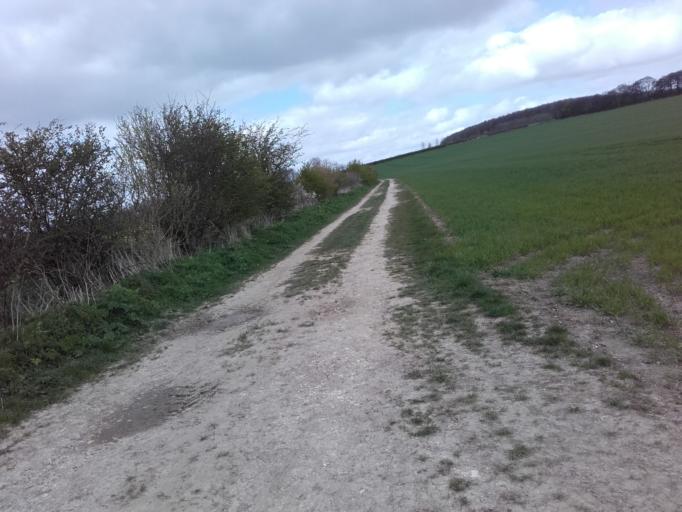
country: GB
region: England
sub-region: East Riding of Yorkshire
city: Market Weighton
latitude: 53.8804
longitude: -0.6628
